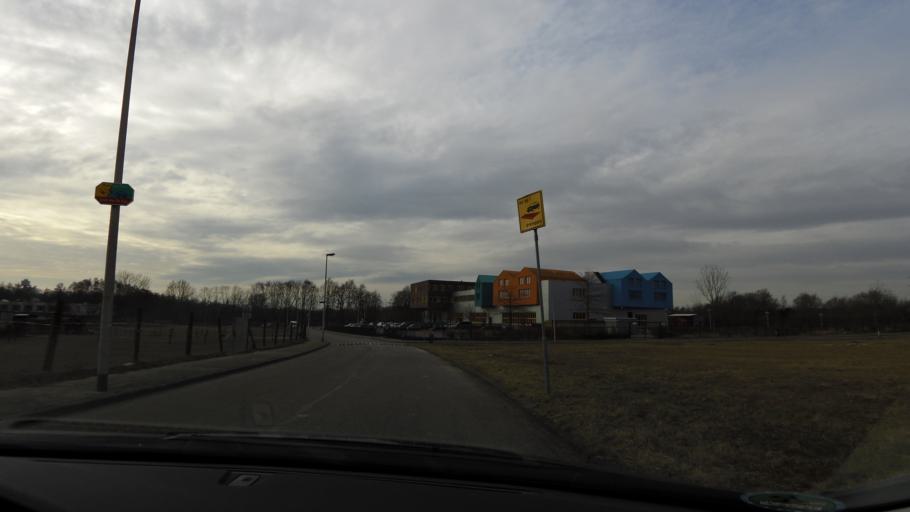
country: NL
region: Limburg
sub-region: Gemeente Brunssum
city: Brunssum
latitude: 50.9288
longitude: 5.9552
